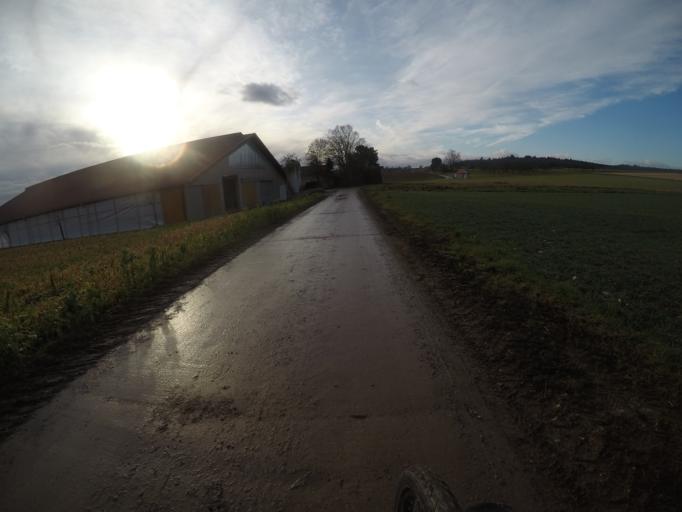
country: DE
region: Baden-Wuerttemberg
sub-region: Regierungsbezirk Stuttgart
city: Unterensingen
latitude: 48.6652
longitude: 9.3427
